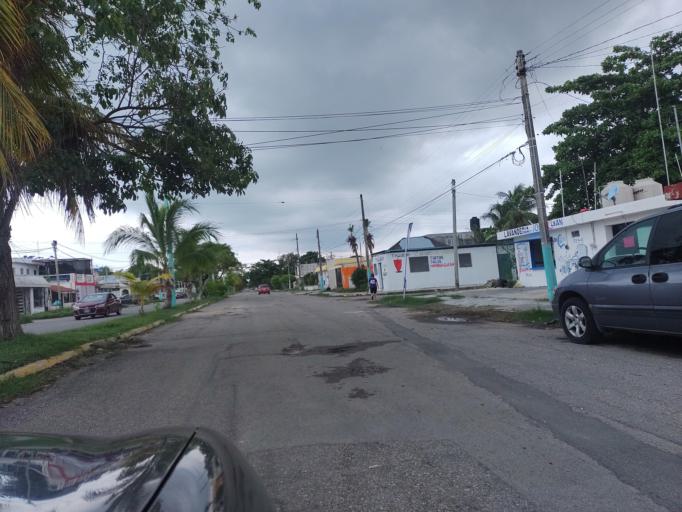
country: MX
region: Quintana Roo
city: Chetumal
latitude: 18.5198
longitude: -88.2760
